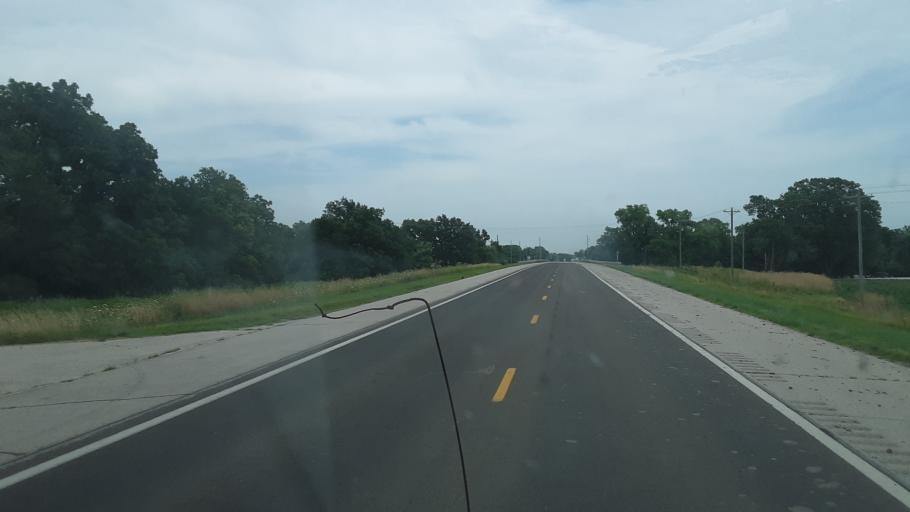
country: US
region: Kansas
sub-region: Allen County
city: Iola
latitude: 37.9220
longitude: -95.4298
